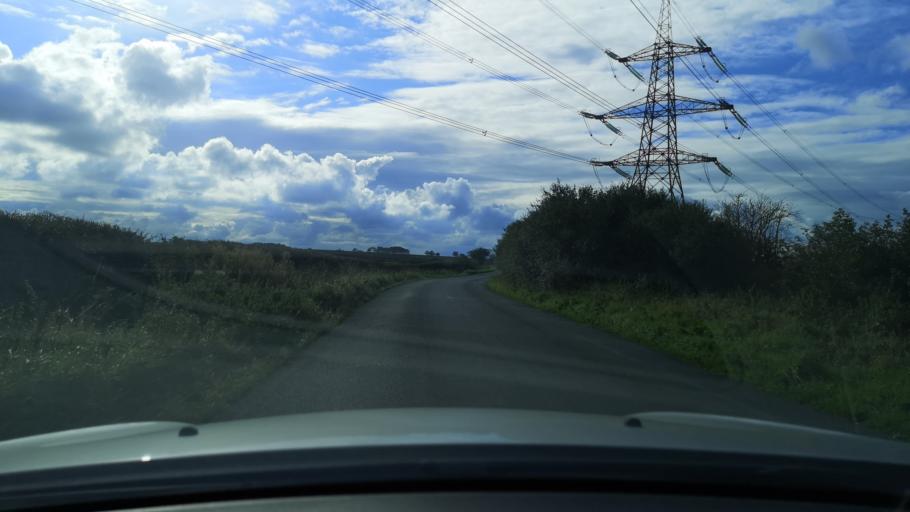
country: GB
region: England
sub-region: East Riding of Yorkshire
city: Walkington
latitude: 53.8291
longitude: -0.5068
